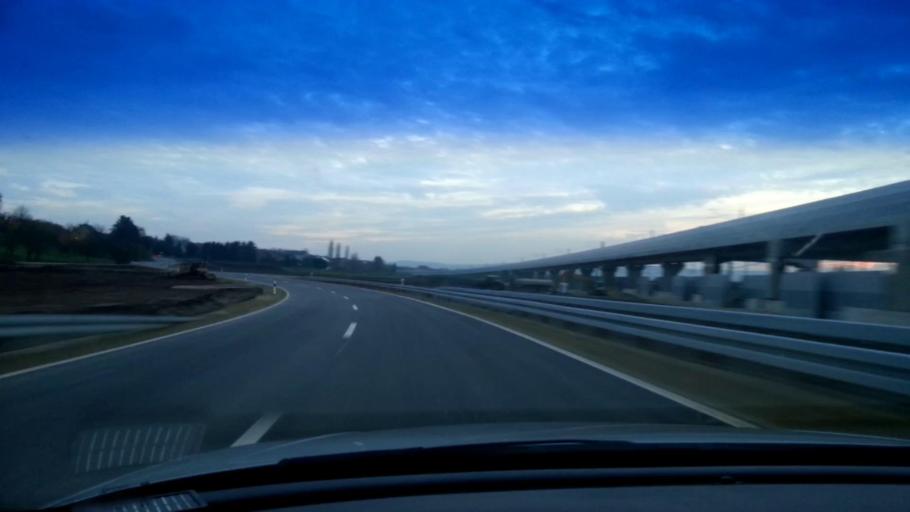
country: DE
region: Bavaria
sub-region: Upper Franconia
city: Breitengussbach
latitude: 49.9823
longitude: 10.8956
